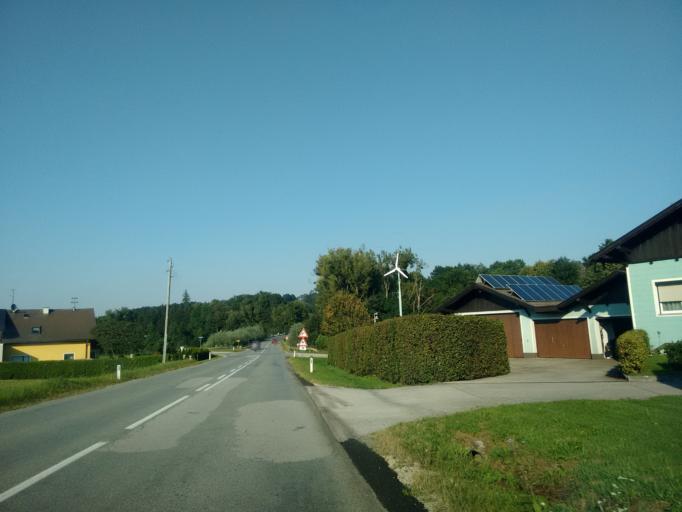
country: AT
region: Upper Austria
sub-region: Wels-Land
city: Sattledt
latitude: 48.0079
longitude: 14.0429
